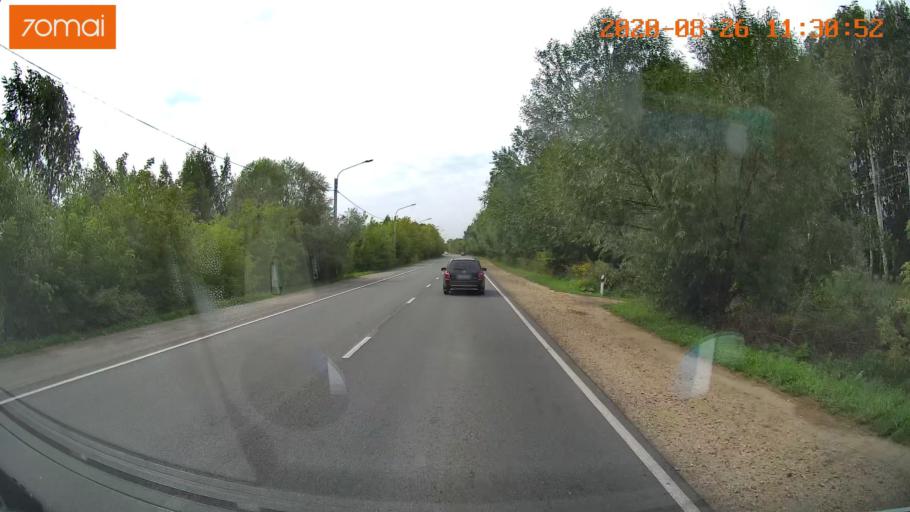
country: RU
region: Rjazan
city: Shilovo
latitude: 54.3119
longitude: 40.8783
